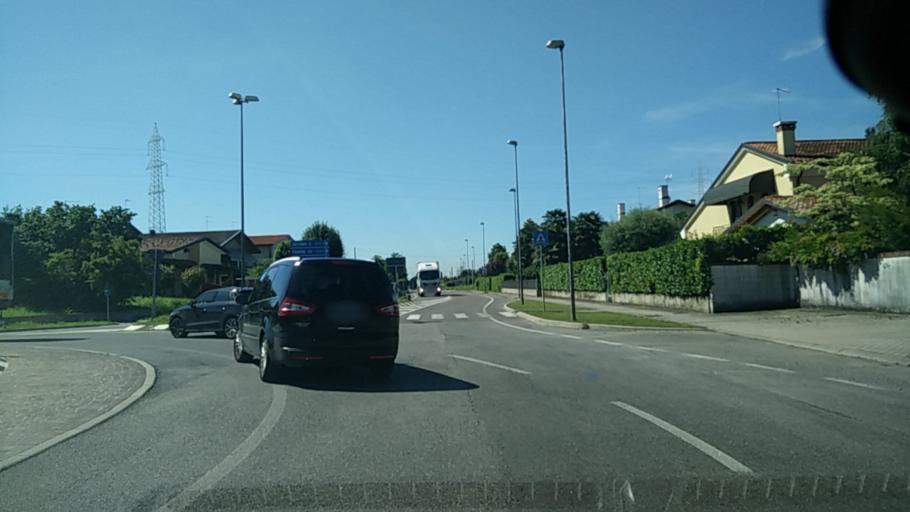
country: IT
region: Veneto
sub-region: Provincia di Venezia
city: Scorze
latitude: 45.5674
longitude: 12.1146
